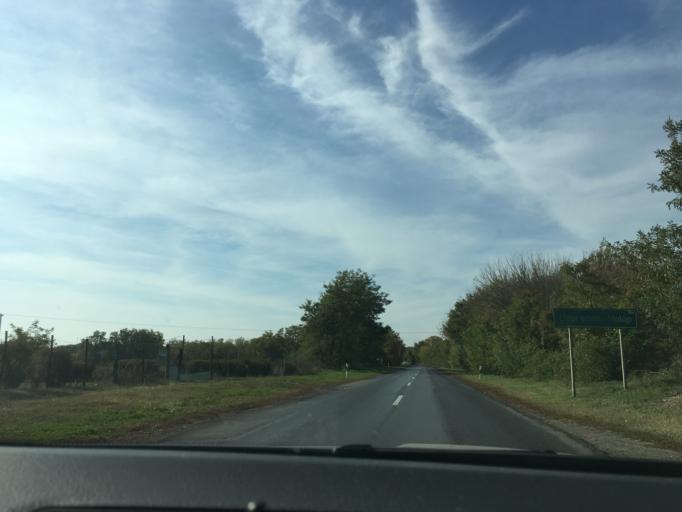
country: HU
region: Hajdu-Bihar
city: Vamospercs
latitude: 47.5291
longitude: 21.8323
